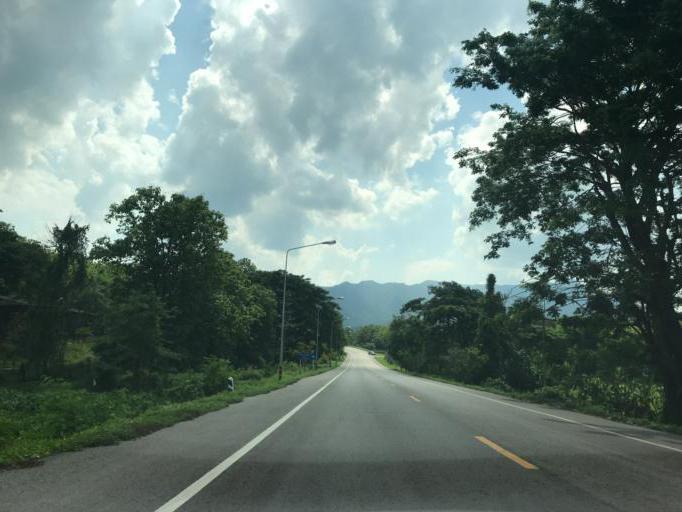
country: TH
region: Phayao
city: Phayao
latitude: 19.0918
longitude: 99.8312
